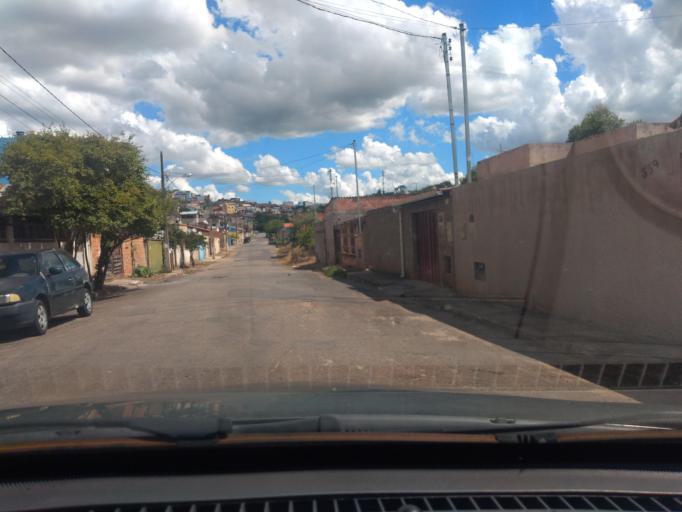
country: BR
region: Minas Gerais
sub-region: Tres Coracoes
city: Tres Coracoes
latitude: -21.6830
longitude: -45.2513
